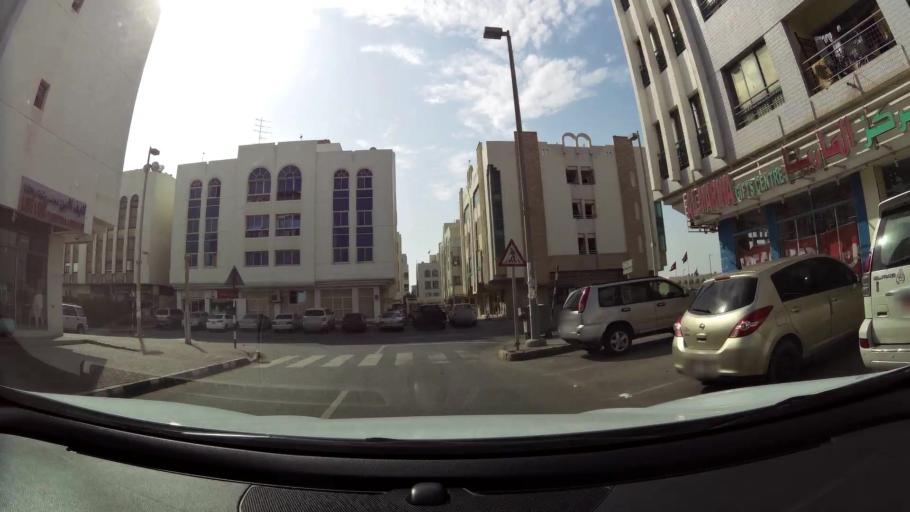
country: AE
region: Abu Dhabi
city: Abu Dhabi
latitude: 24.3282
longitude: 54.5339
